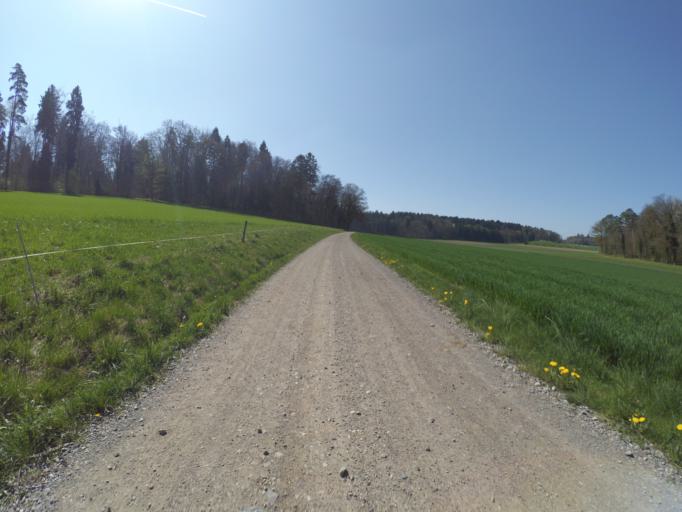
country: CH
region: Thurgau
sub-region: Frauenfeld District
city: Diessenhofen
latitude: 47.6524
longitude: 8.7442
